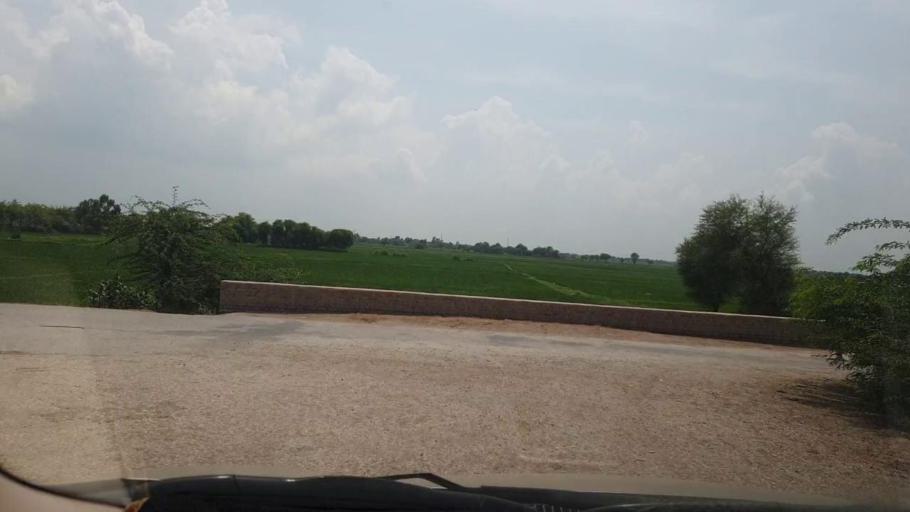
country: PK
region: Sindh
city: Larkana
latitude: 27.6037
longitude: 68.1242
